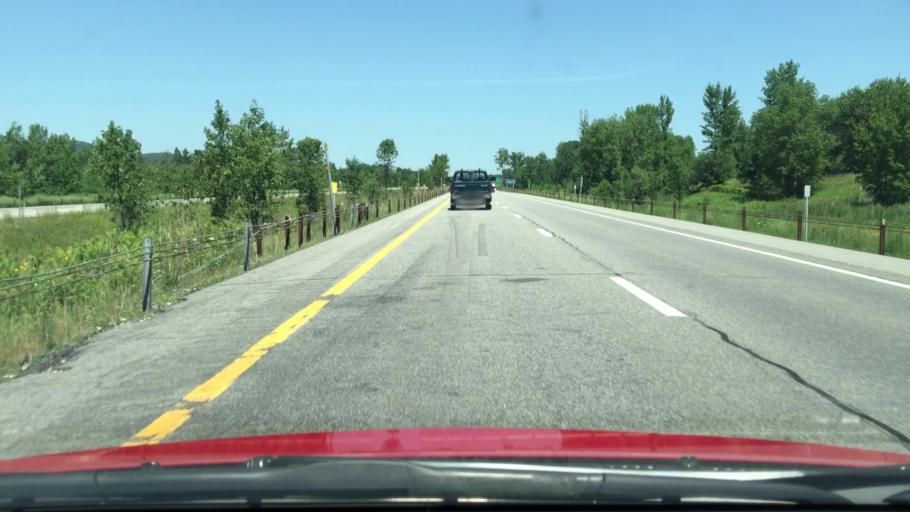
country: US
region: New York
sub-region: Essex County
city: Keeseville
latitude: 44.4341
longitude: -73.4915
